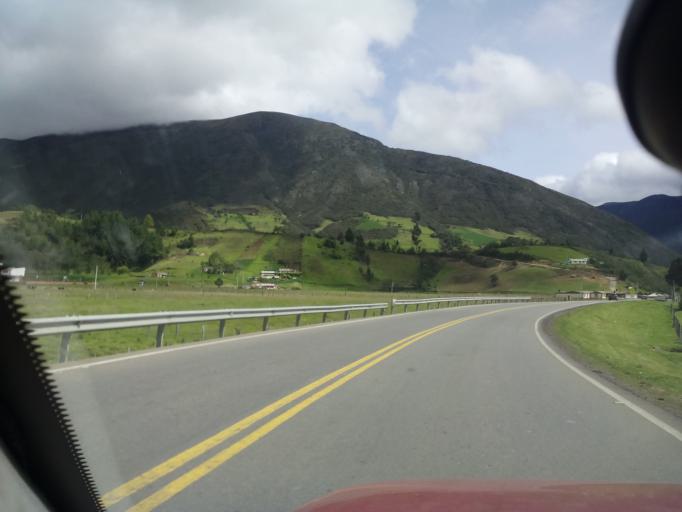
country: CO
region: Boyaca
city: Arcabuco
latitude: 5.7032
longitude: -73.3712
